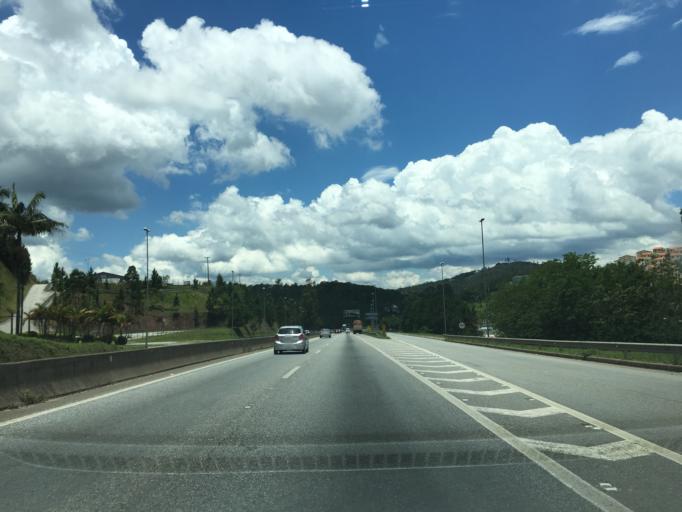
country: BR
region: Sao Paulo
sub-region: Mairipora
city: Mairipora
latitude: -23.2615
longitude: -46.5874
